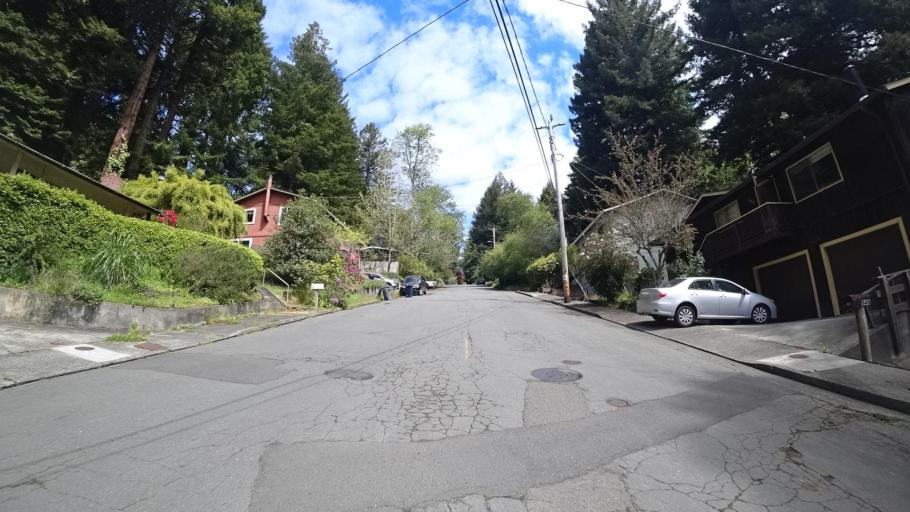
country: US
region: California
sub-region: Humboldt County
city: Arcata
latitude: 40.8618
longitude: -124.0683
